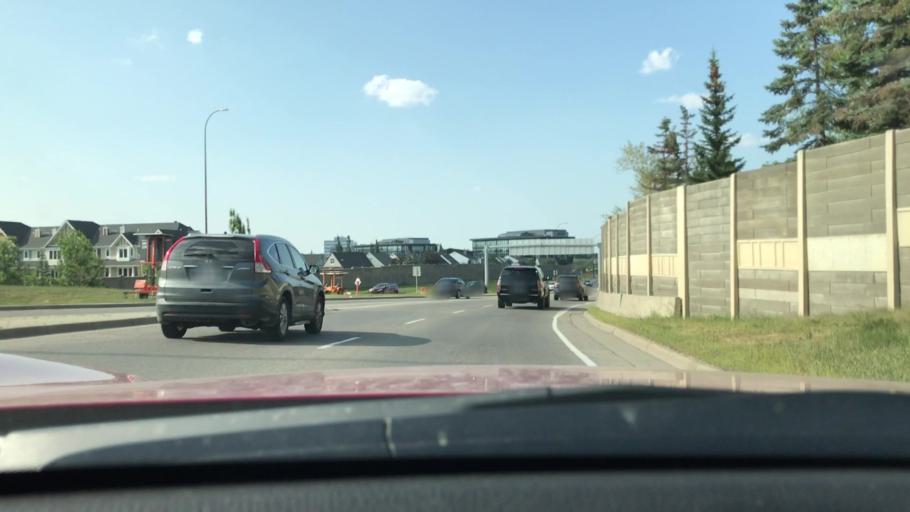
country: CA
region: Alberta
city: Calgary
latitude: 51.0014
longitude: -114.1178
